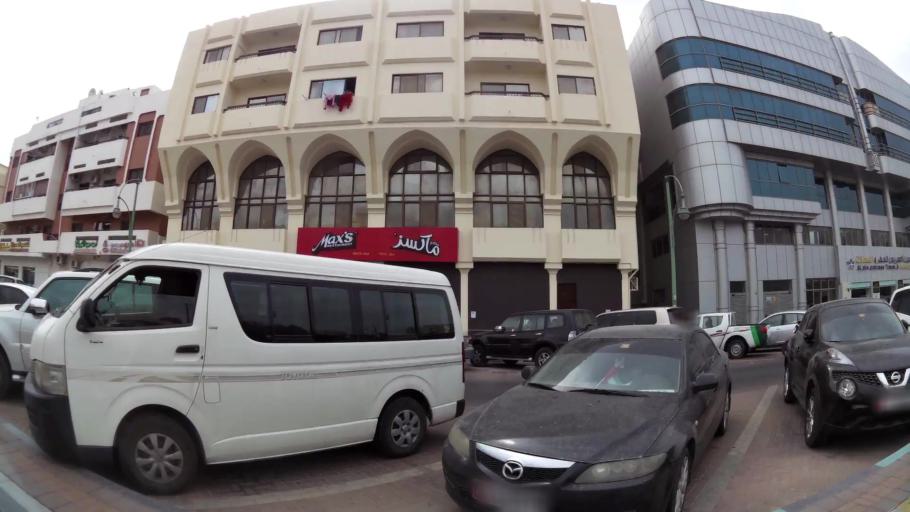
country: AE
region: Abu Dhabi
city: Al Ain
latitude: 24.2218
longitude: 55.7620
